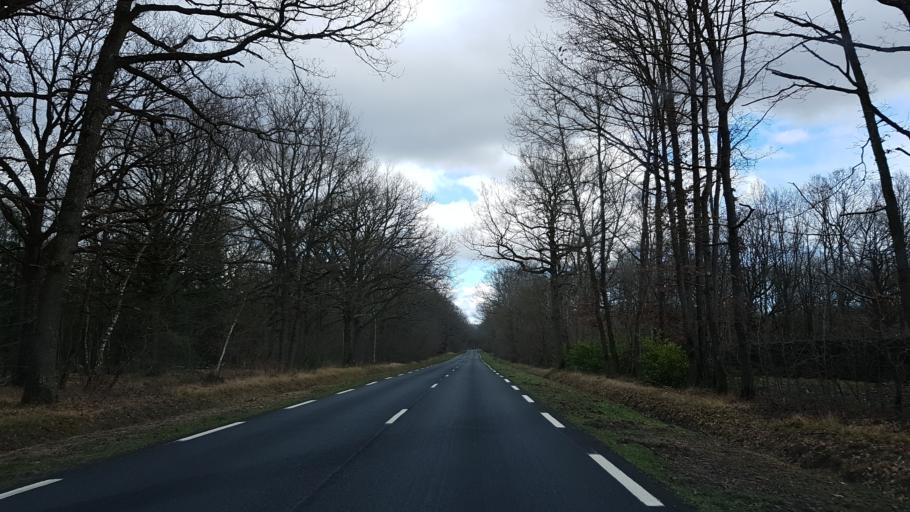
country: FR
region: Ile-de-France
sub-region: Departement des Yvelines
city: Sonchamp
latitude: 48.6301
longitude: 1.8869
